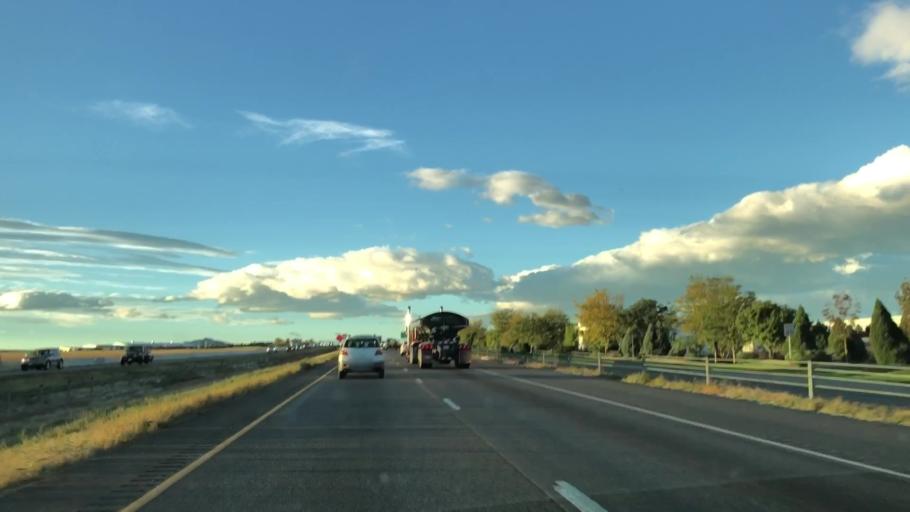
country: US
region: Colorado
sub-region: Weld County
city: Windsor
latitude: 40.4557
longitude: -104.9930
